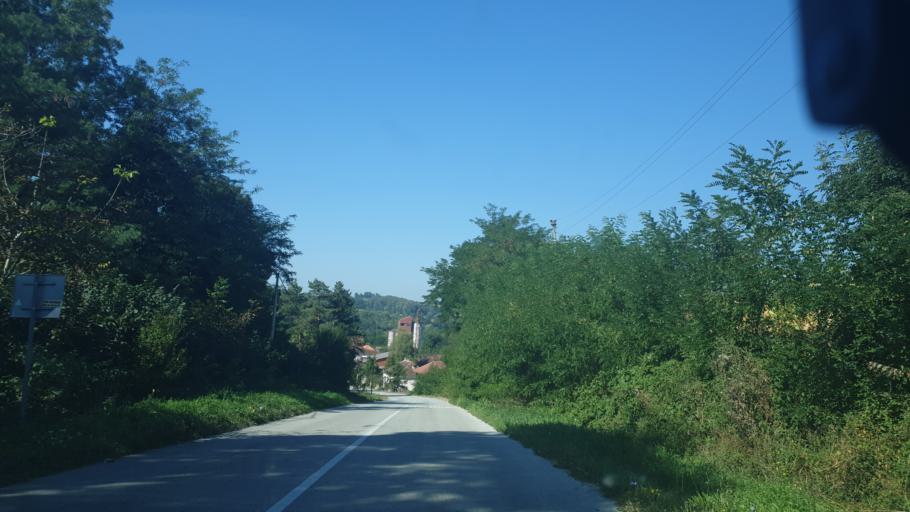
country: RS
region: Central Serbia
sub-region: Kolubarski Okrug
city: Mionica
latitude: 44.2862
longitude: 20.1178
